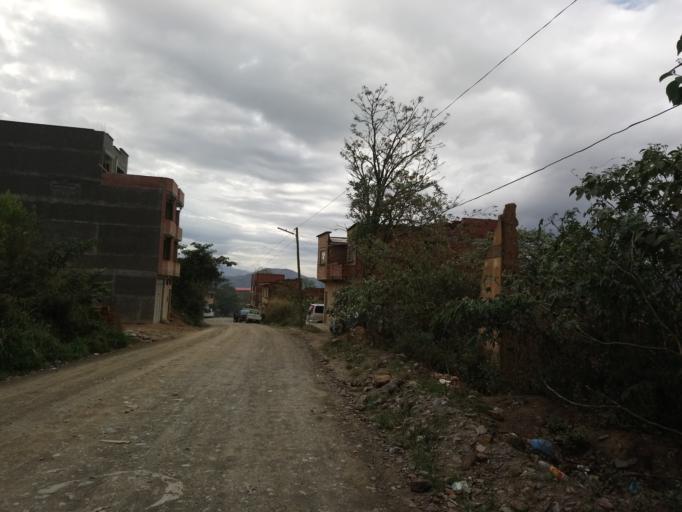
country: BO
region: La Paz
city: Coripata
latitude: -16.2714
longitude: -67.6372
